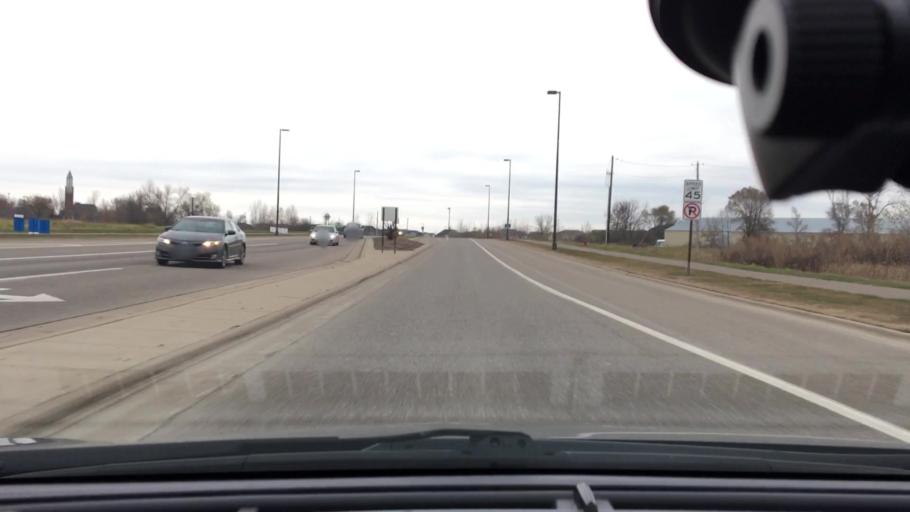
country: US
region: Minnesota
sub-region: Hennepin County
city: Corcoran
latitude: 45.0864
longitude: -93.5163
